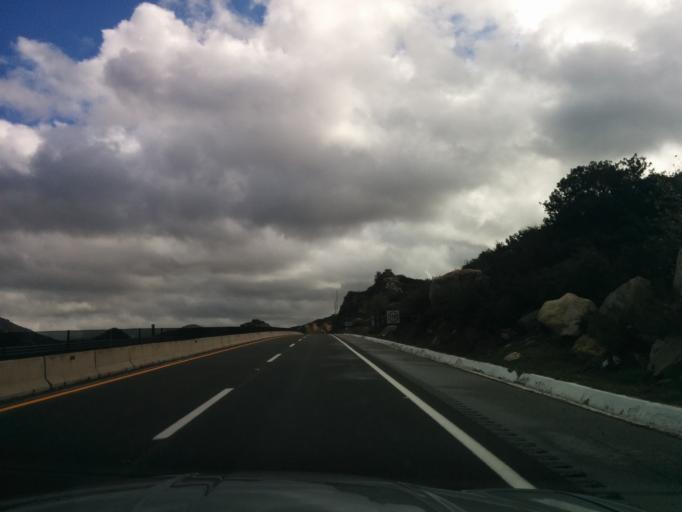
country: MX
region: Baja California
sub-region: Tecate
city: Hacienda Tecate
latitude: 32.5586
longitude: -116.5569
